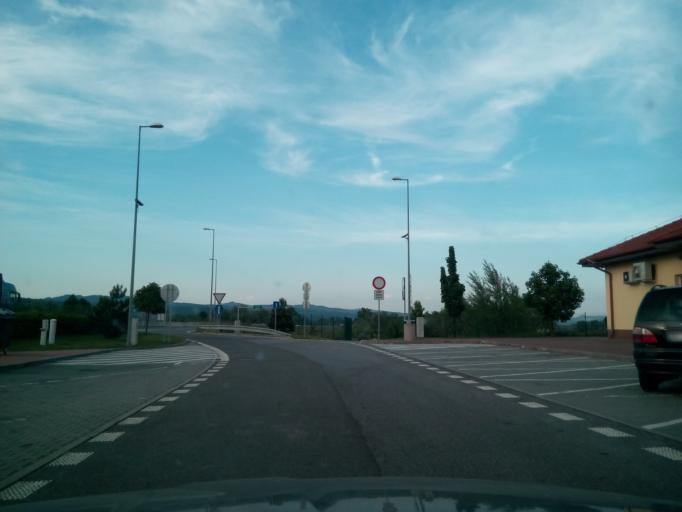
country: SK
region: Zilinsky
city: Bytca
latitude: 49.2033
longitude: 18.5236
